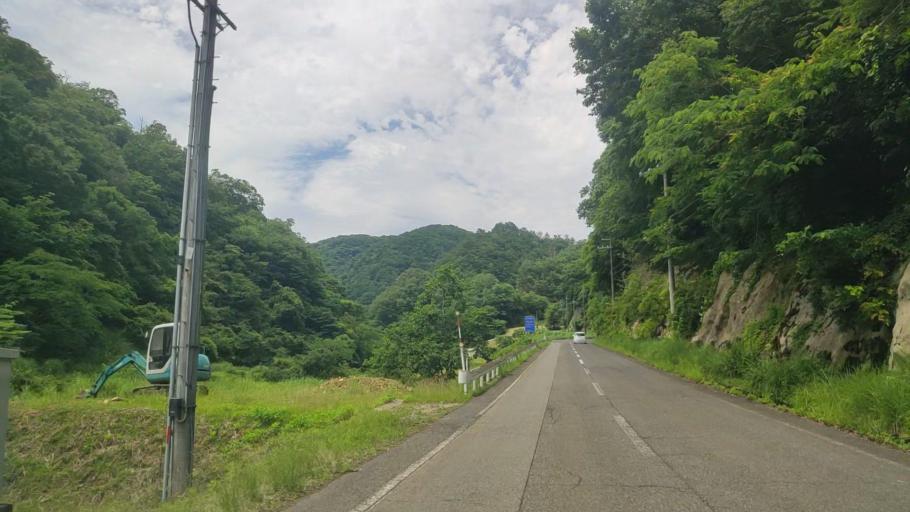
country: JP
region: Hyogo
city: Toyooka
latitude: 35.5227
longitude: 134.6978
